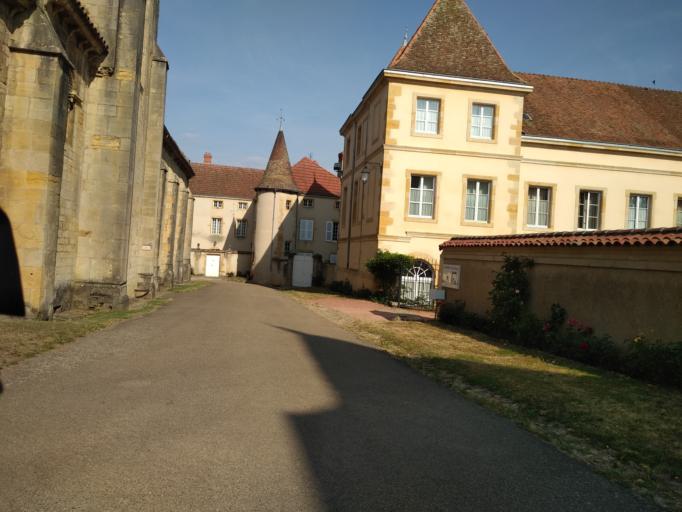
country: FR
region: Bourgogne
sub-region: Departement de Saone-et-Loire
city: Marcigny
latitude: 46.2635
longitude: 4.0874
